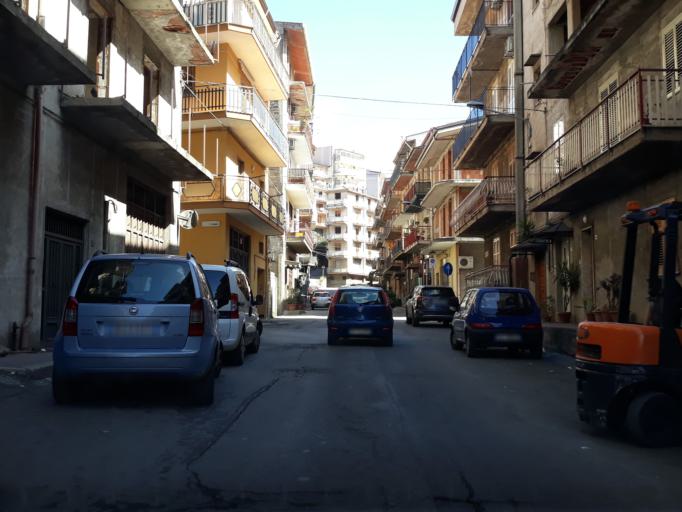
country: IT
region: Sicily
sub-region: Palermo
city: Belmonte Mezzagno
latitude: 38.0469
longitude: 13.3933
